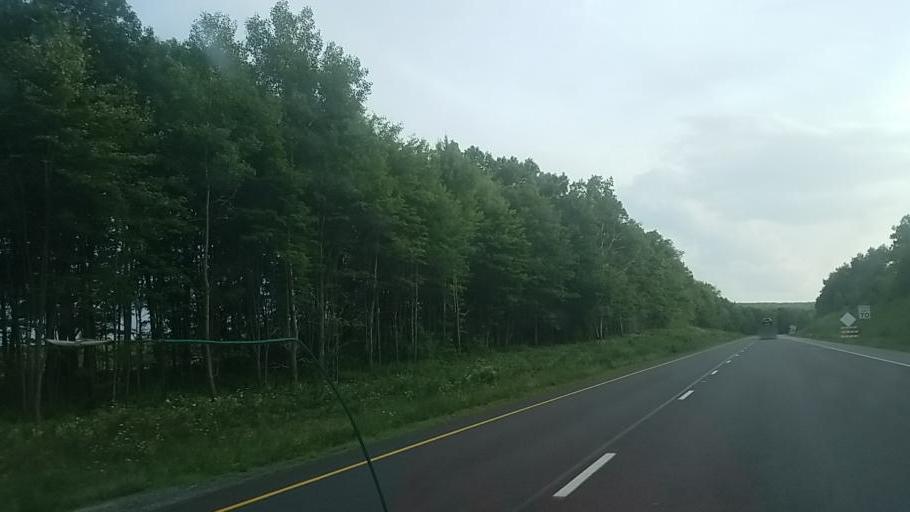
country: US
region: Pennsylvania
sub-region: Centre County
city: Milesburg
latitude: 41.0145
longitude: -77.9579
